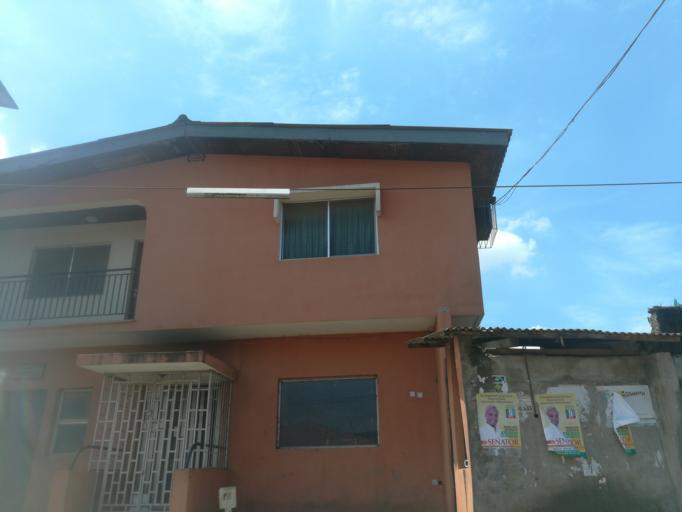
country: NG
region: Lagos
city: Oshodi
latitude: 6.5669
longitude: 3.3353
